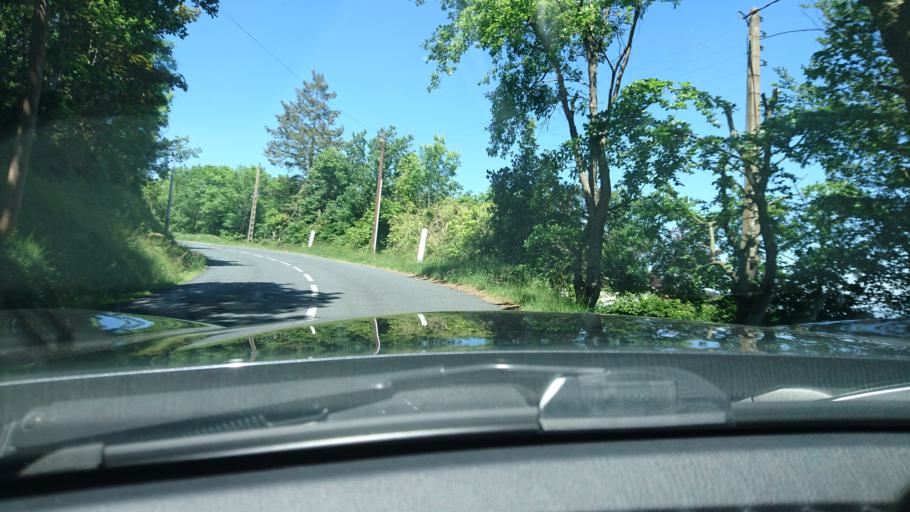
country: FR
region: Rhone-Alpes
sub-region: Departement du Rhone
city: Courzieu
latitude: 45.7109
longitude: 4.5903
